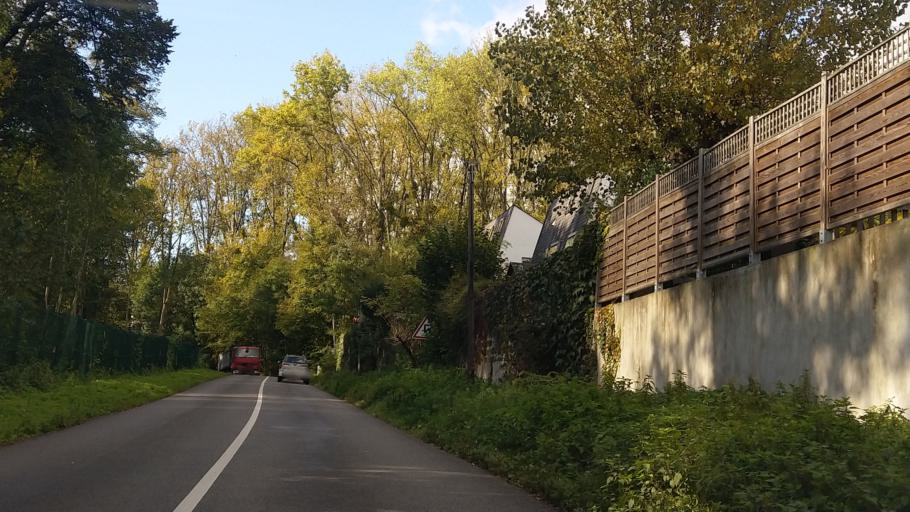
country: FR
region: Ile-de-France
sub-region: Departement du Val-d'Oise
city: Baillet-en-France
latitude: 49.0663
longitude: 2.2997
